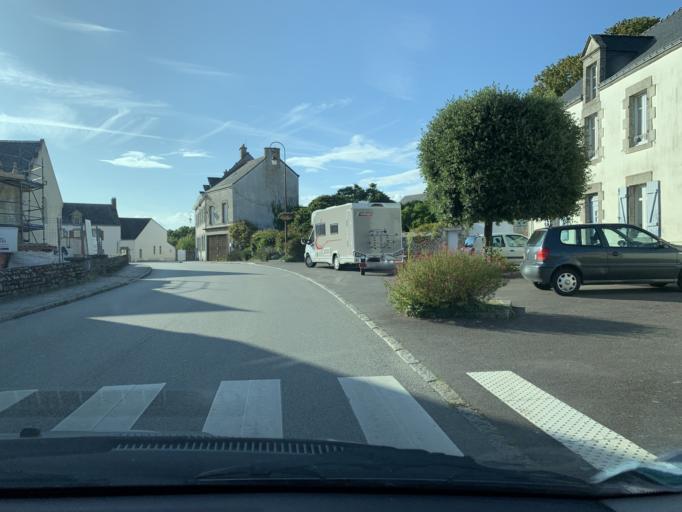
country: FR
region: Brittany
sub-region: Departement du Morbihan
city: Ambon
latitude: 47.5547
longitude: -2.5584
